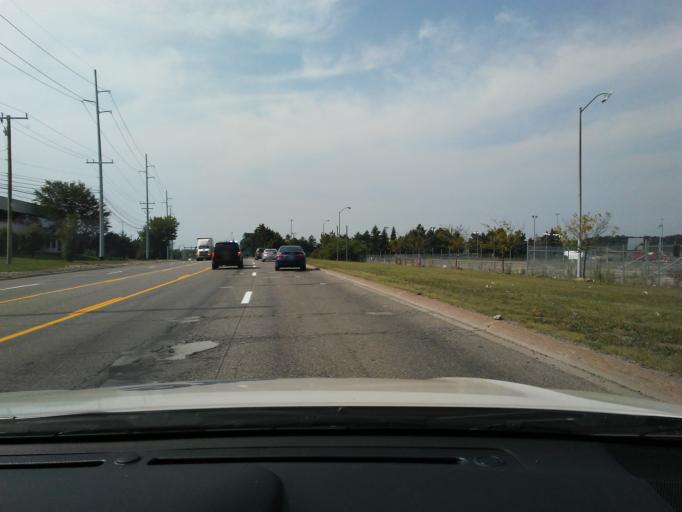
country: US
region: Michigan
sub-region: Oakland County
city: Pontiac
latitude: 42.6467
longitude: -83.2492
